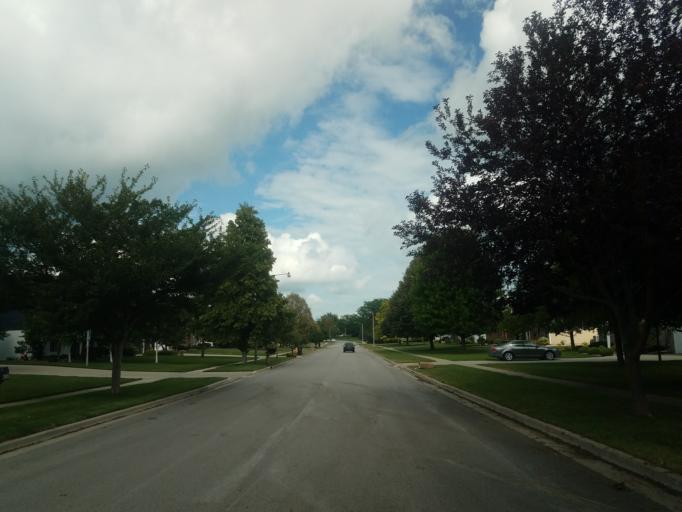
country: US
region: Illinois
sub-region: McLean County
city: Normal
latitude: 40.5073
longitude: -88.9223
